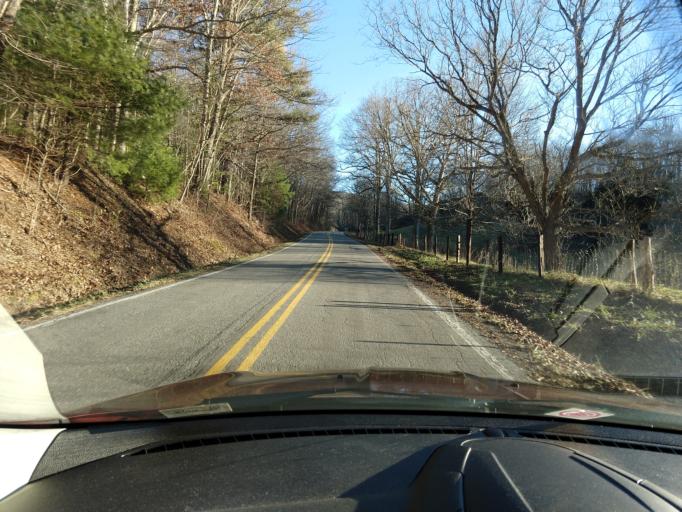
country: US
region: Virginia
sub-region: Alleghany County
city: Clifton Forge
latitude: 37.9046
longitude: -79.8926
